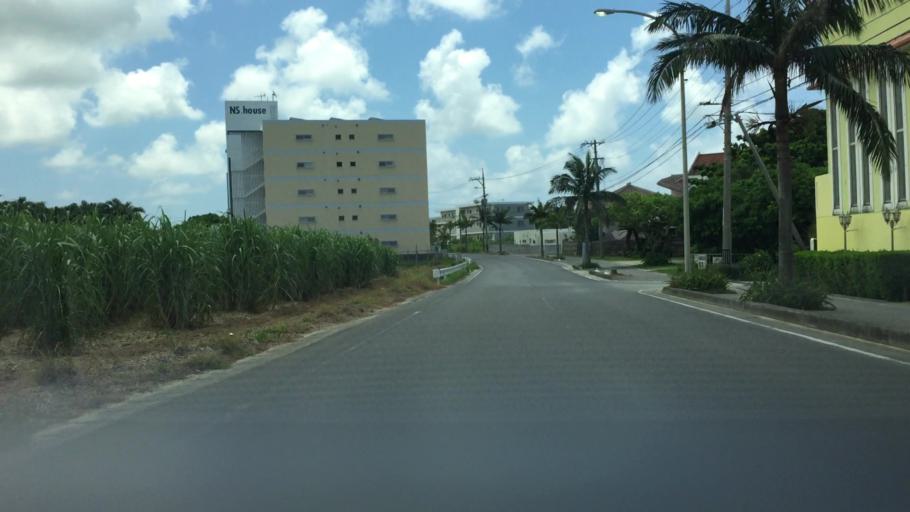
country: JP
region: Okinawa
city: Ishigaki
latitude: 24.3563
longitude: 124.1327
